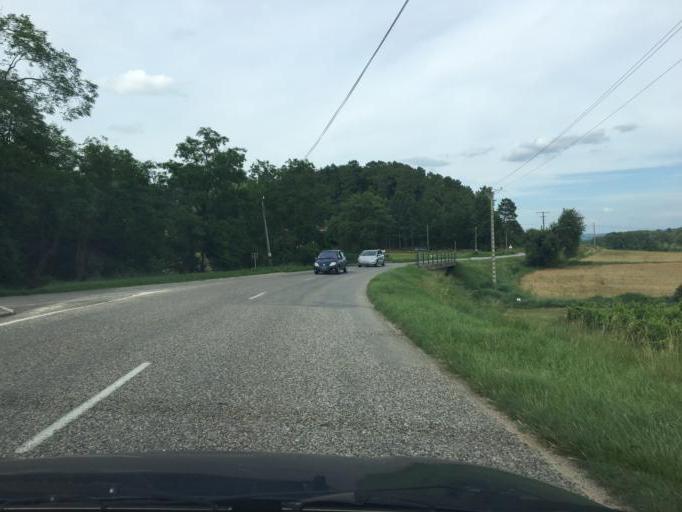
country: FR
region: Rhone-Alpes
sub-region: Departement de la Drome
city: Clerieux
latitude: 45.1087
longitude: 4.9526
